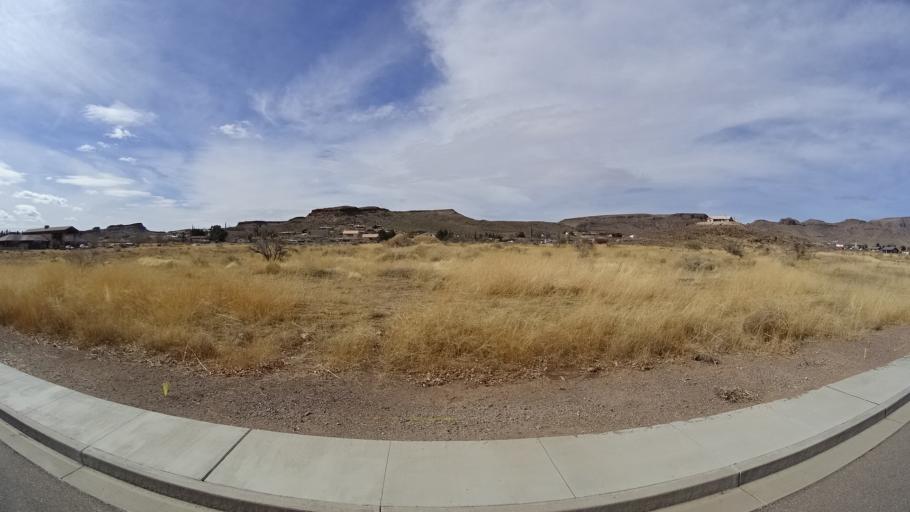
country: US
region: Arizona
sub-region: Mohave County
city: Kingman
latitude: 35.2260
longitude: -114.0422
